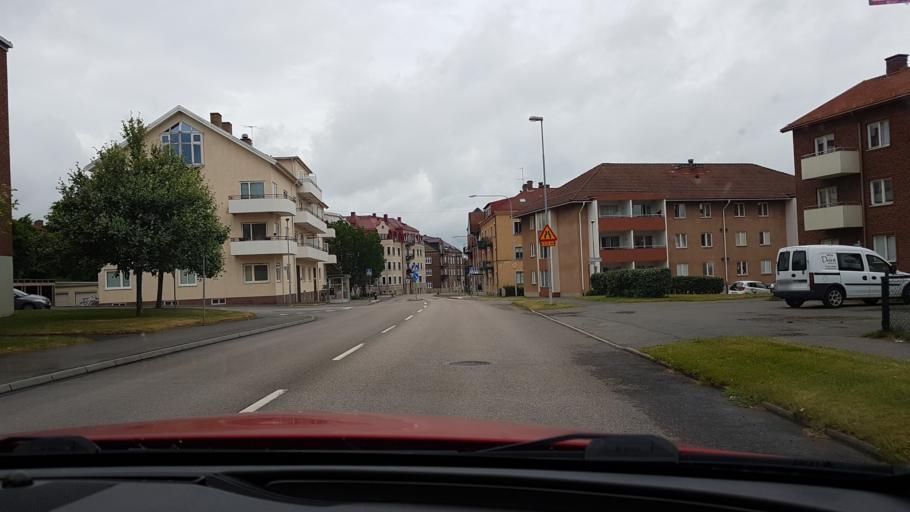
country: SE
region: Vaestra Goetaland
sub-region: Skovde Kommun
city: Skoevde
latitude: 58.3824
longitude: 13.8432
